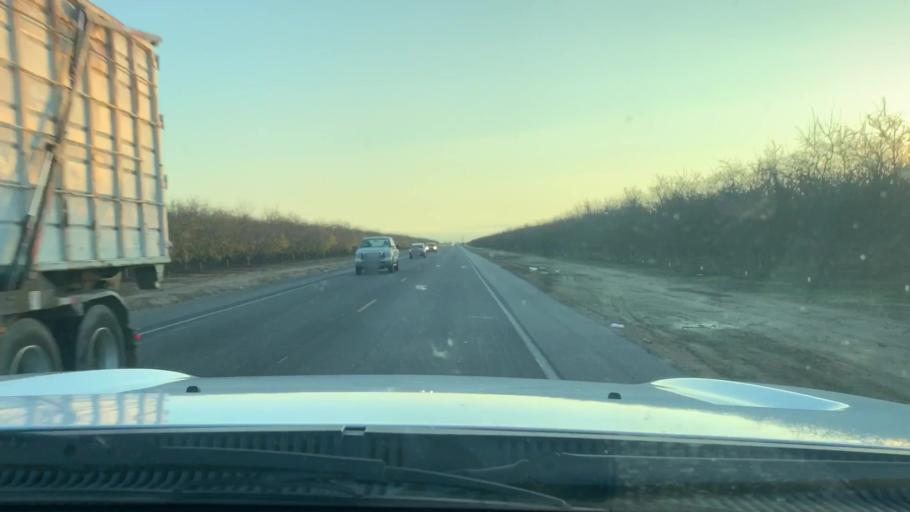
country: US
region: California
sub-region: Kern County
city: Wasco
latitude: 35.5003
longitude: -119.3982
